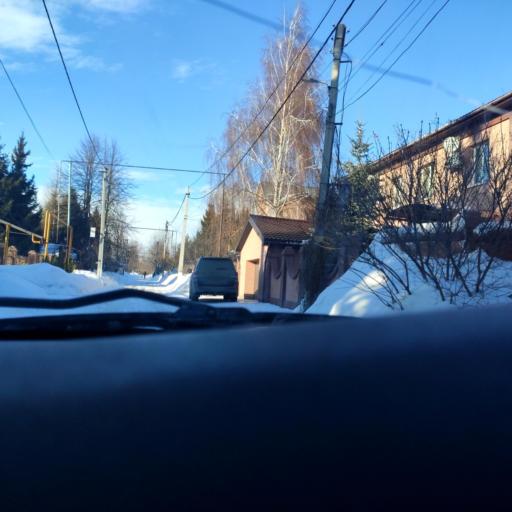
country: RU
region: Samara
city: Podstepki
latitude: 53.5132
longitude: 49.1565
